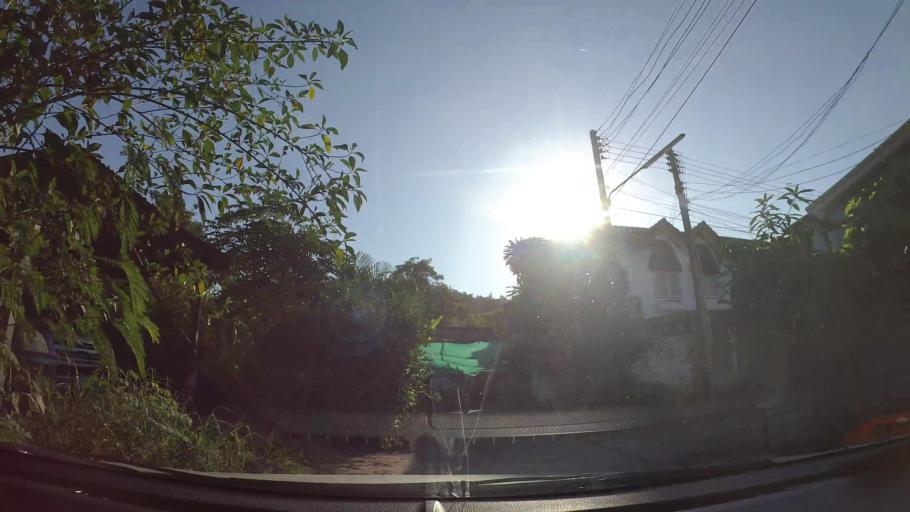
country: TH
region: Chon Buri
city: Si Racha
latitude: 13.1533
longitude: 100.9327
